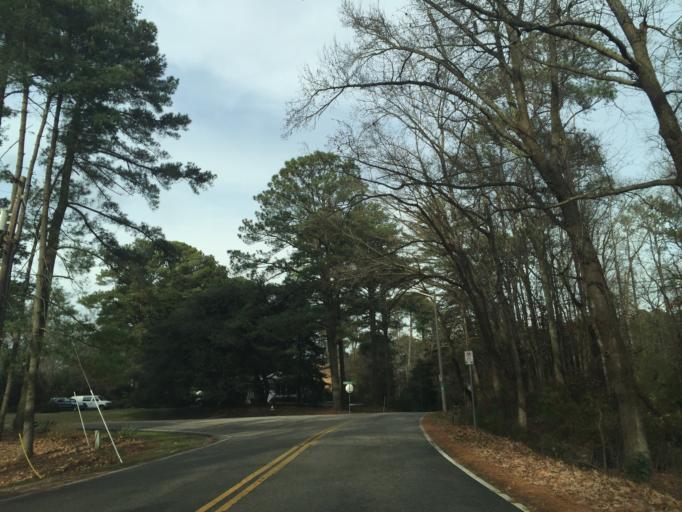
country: US
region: Virginia
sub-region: City of Newport News
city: Newport News
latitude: 37.0436
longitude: -76.4913
